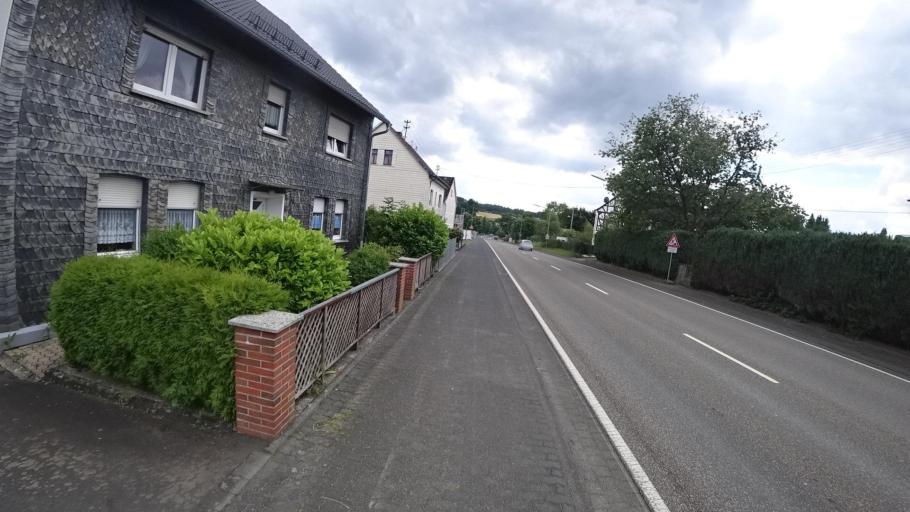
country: DE
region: Rheinland-Pfalz
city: Mammelzen
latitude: 50.7041
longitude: 7.6685
